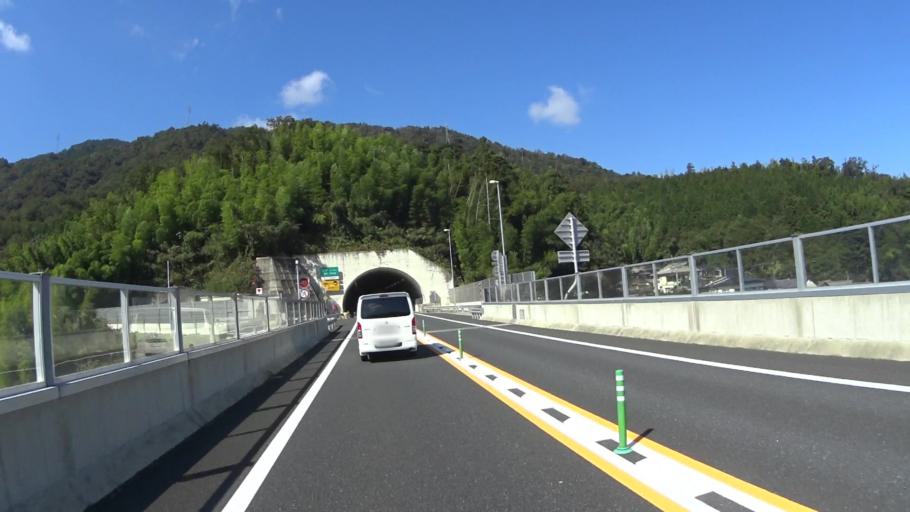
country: JP
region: Kyoto
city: Miyazu
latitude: 35.5193
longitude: 135.1860
